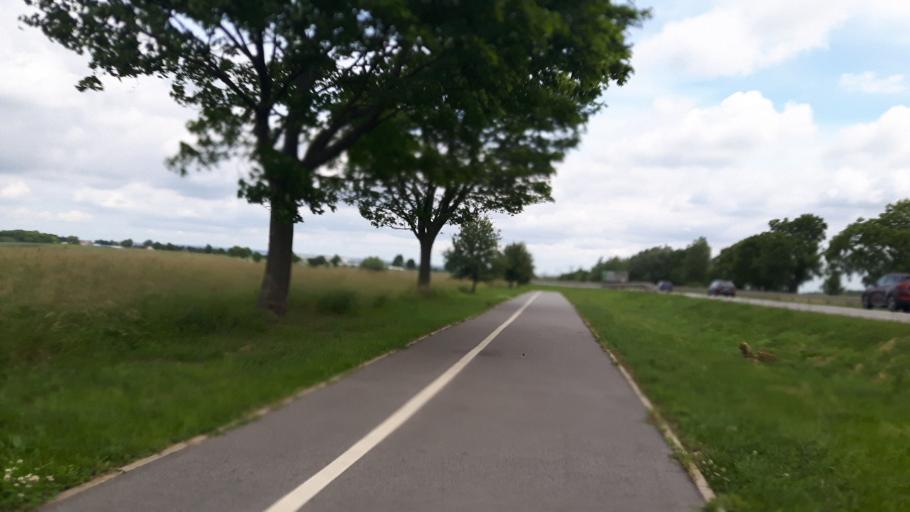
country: PL
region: West Pomeranian Voivodeship
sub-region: Powiat policki
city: Przeclaw
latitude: 53.3623
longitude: 14.4702
